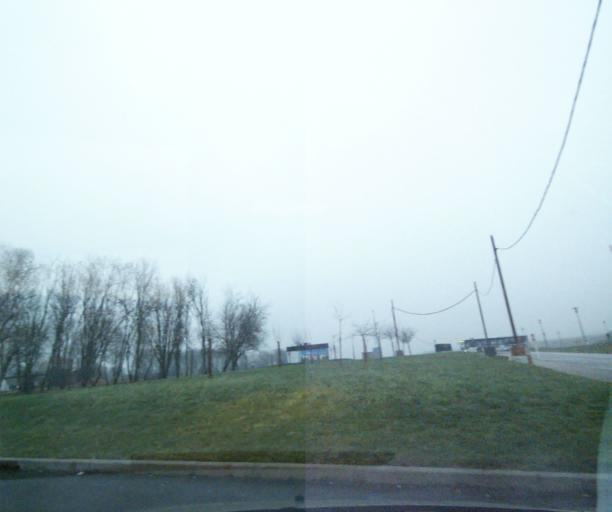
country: FR
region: Ile-de-France
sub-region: Departement de Seine-et-Marne
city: Othis
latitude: 49.0697
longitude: 2.6778
